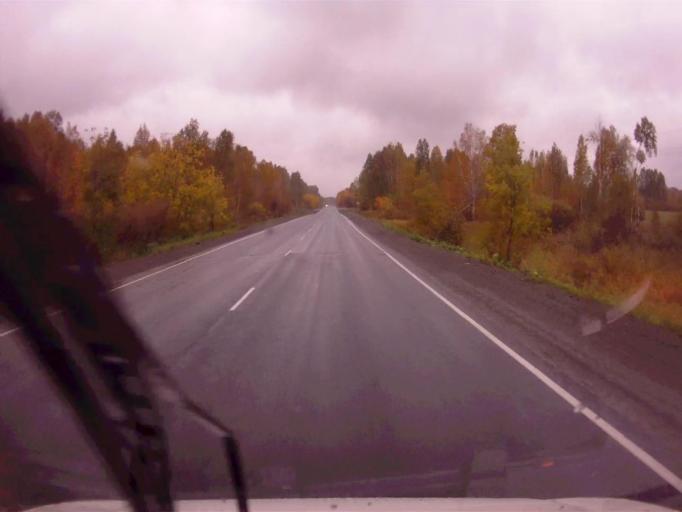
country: RU
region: Chelyabinsk
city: Argayash
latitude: 55.4788
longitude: 60.7889
